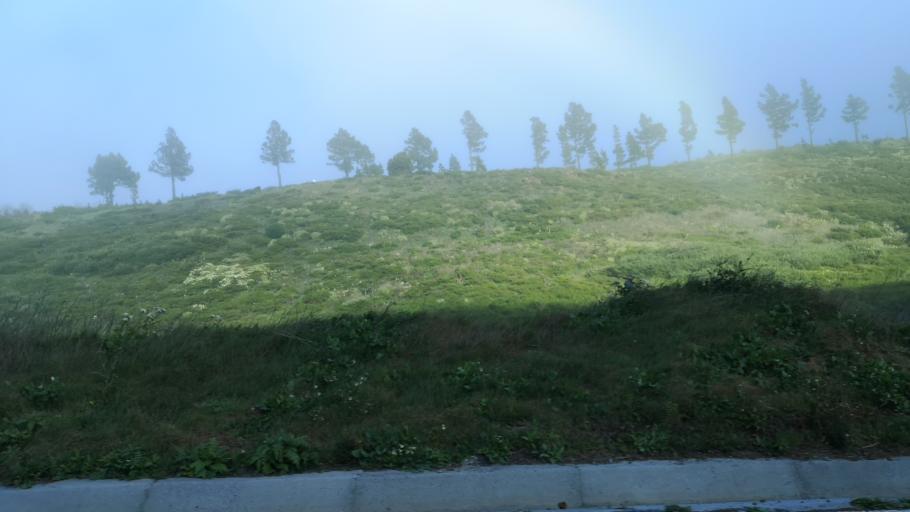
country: ES
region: Canary Islands
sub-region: Provincia de Santa Cruz de Tenerife
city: Alajero
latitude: 28.0973
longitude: -17.2481
